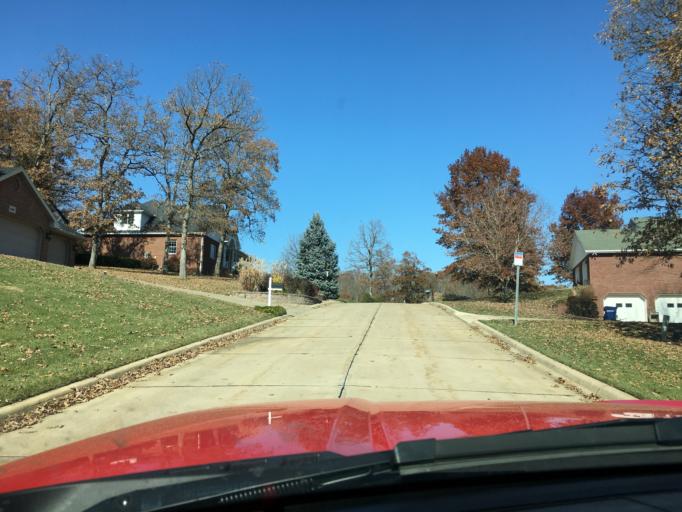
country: US
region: Missouri
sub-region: Cole County
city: Wardsville
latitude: 38.4812
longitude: -92.1816
